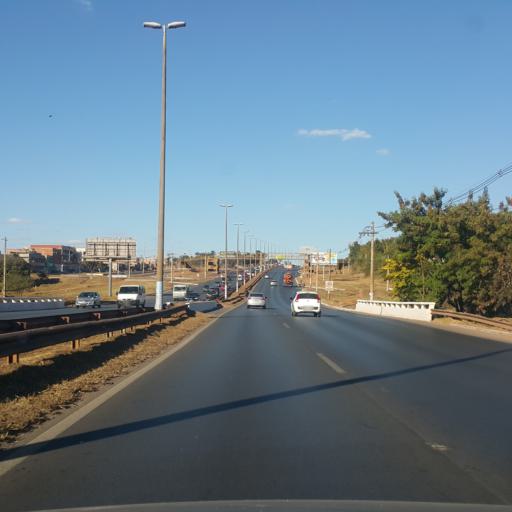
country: BR
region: Federal District
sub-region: Brasilia
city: Brasilia
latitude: -15.7863
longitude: -48.0036
